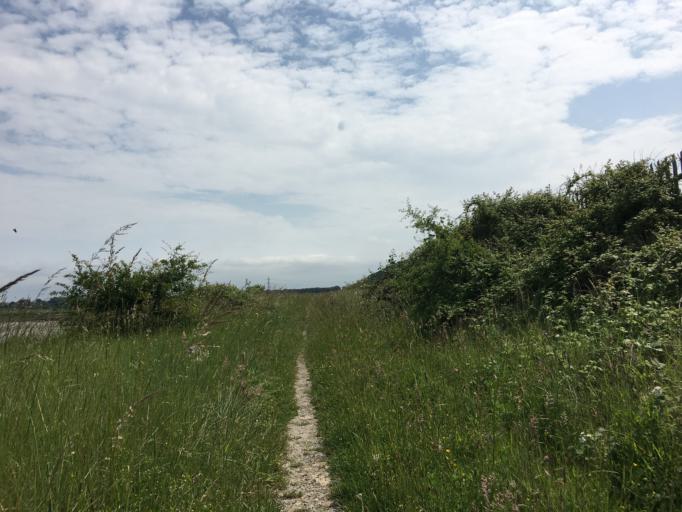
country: GB
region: England
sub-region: Kent
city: Sittingbourne
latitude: 51.3639
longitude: 0.7640
